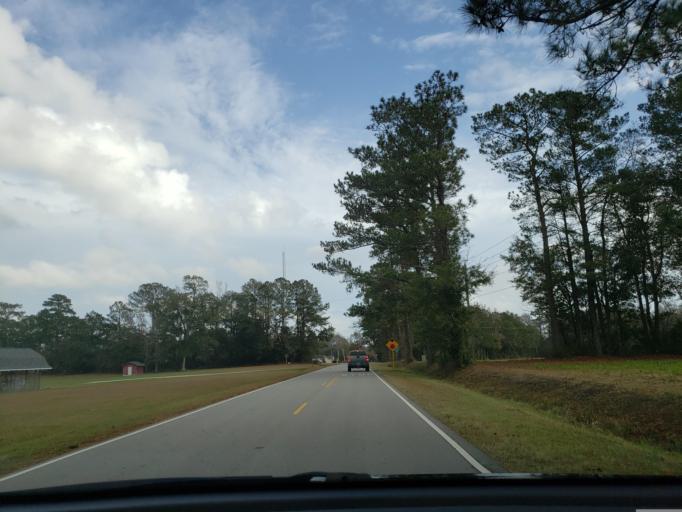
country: US
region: North Carolina
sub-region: Onslow County
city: Jacksonville
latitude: 34.6950
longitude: -77.5538
